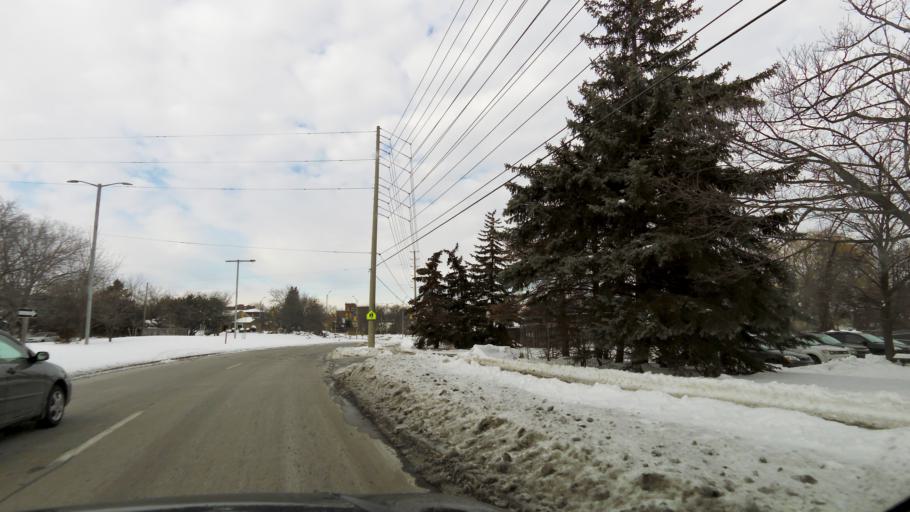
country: CA
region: Ontario
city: Mississauga
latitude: 43.5337
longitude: -79.6780
